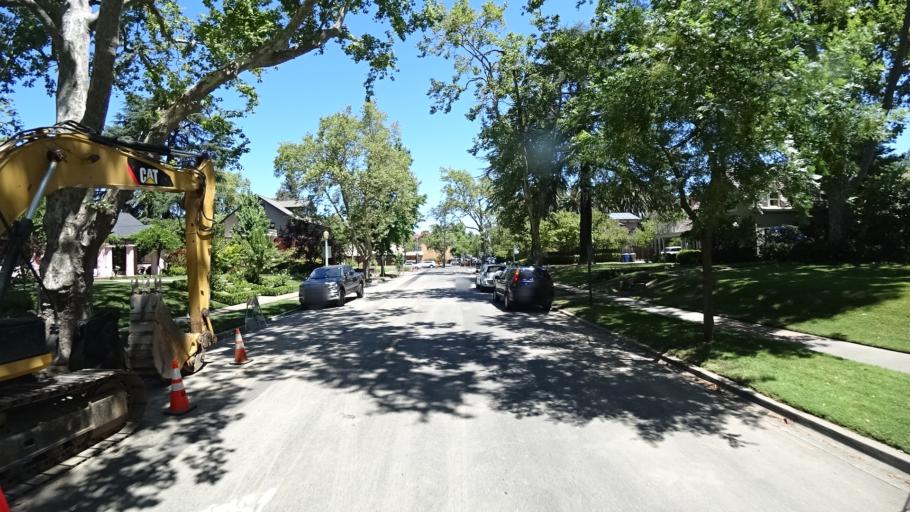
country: US
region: California
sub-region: Sacramento County
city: Sacramento
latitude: 38.5640
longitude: -121.4565
